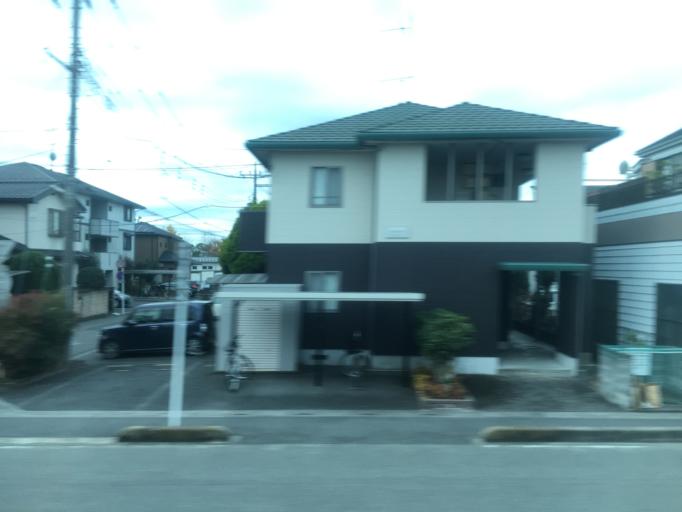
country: JP
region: Saitama
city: Okegawa
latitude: 35.9801
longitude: 139.5824
